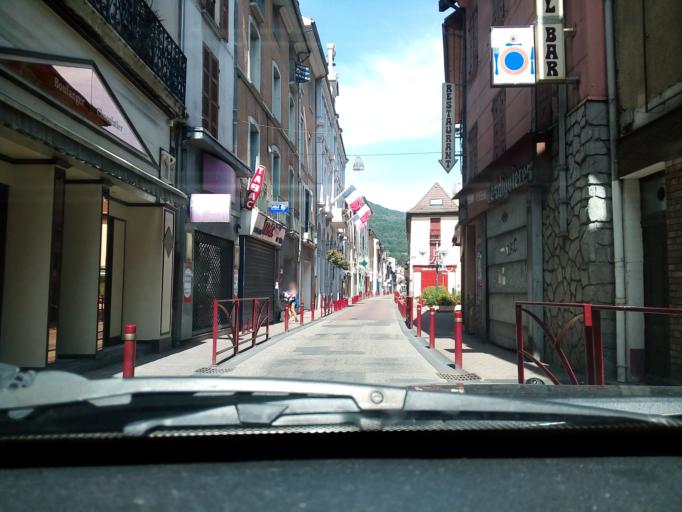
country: FR
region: Rhone-Alpes
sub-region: Departement de l'Isere
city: Vizille
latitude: 45.0768
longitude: 5.7726
